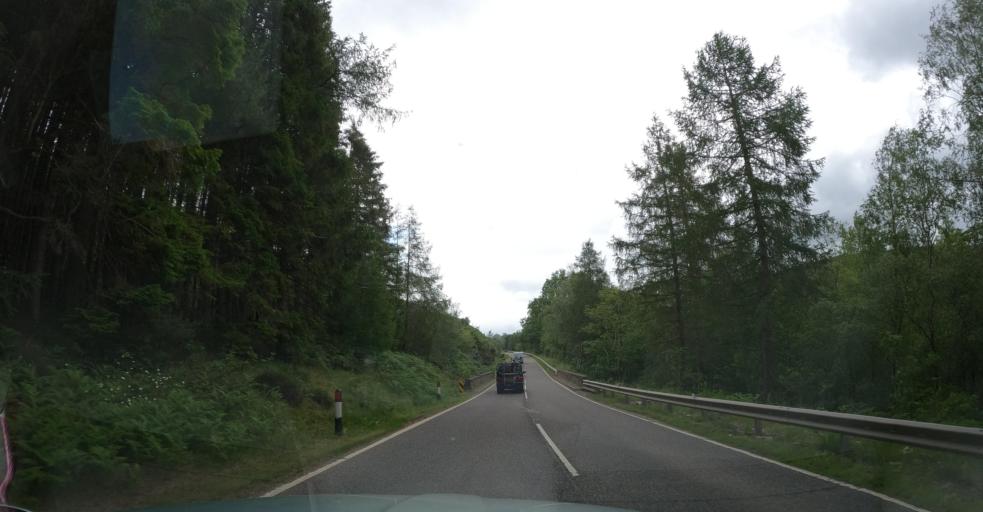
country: GB
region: Scotland
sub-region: Highland
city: Ullapool
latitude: 57.7622
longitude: -5.0306
